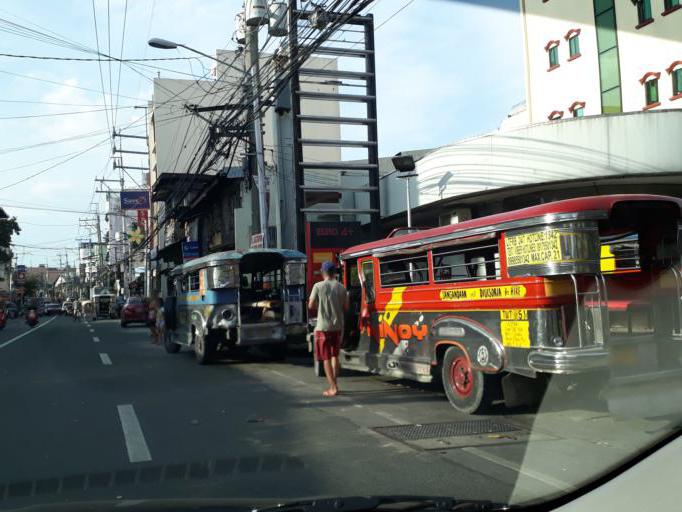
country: PH
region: Metro Manila
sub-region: Caloocan City
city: Niugan
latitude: 14.6394
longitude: 120.9757
